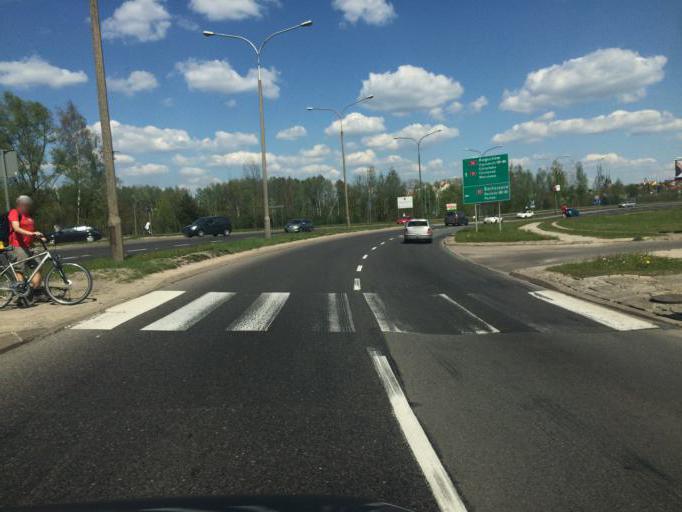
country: PL
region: Warmian-Masurian Voivodeship
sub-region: Olsztyn
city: Kortowo
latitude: 53.7744
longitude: 20.4508
